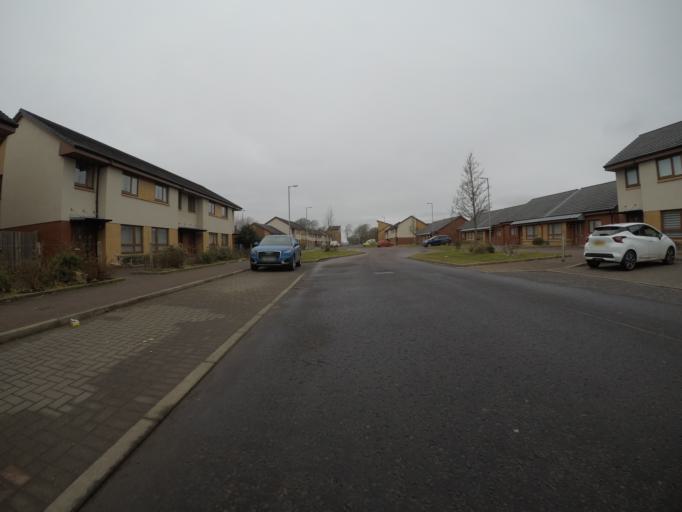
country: GB
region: Scotland
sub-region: North Ayrshire
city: Irvine
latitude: 55.6258
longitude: -4.6704
